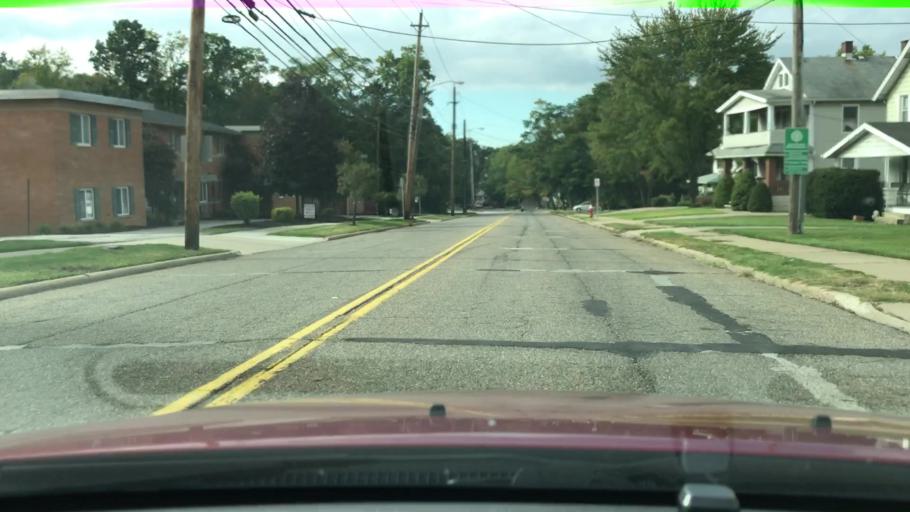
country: US
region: Ohio
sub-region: Cuyahoga County
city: Bedford
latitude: 41.3831
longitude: -81.5281
